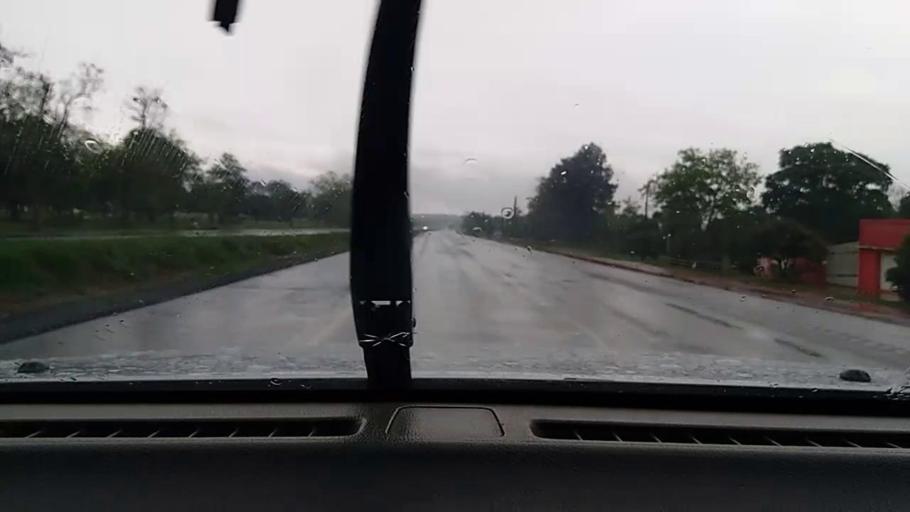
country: PY
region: Caaguazu
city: Repatriacion
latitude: -25.4607
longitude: -55.9240
